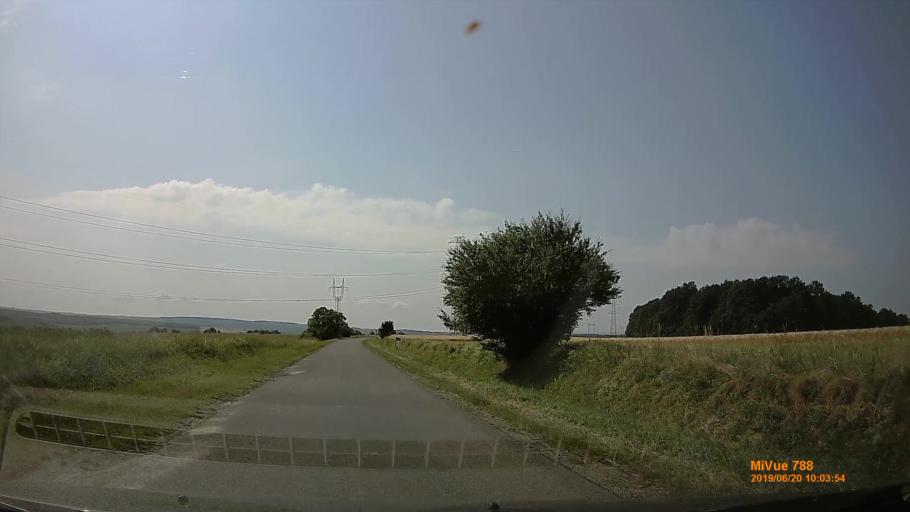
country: HU
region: Baranya
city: Mecseknadasd
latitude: 46.1941
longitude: 18.4632
